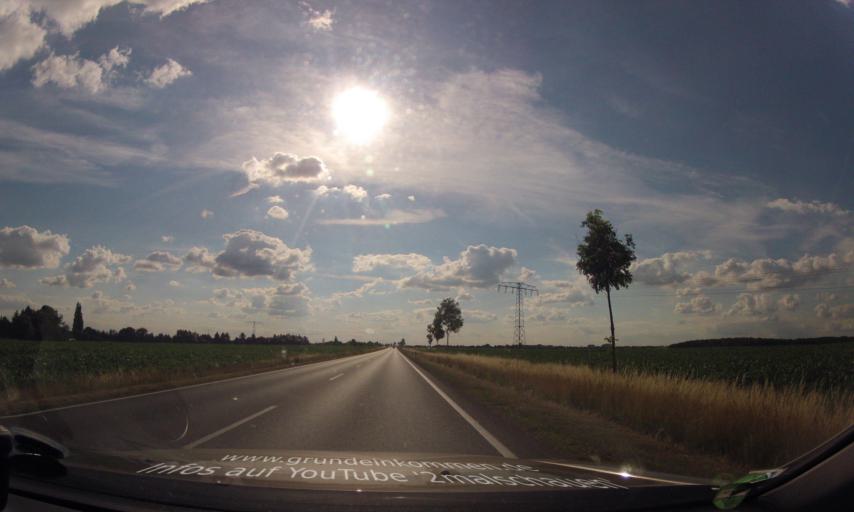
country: DE
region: Saxony
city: Brandis
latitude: 51.3612
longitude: 12.5928
